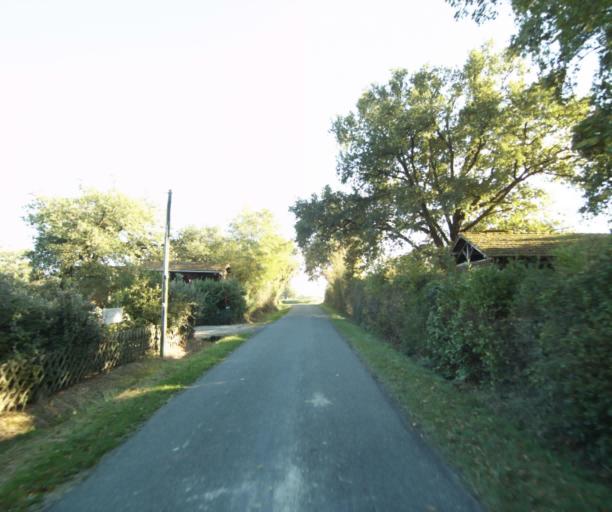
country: FR
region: Midi-Pyrenees
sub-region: Departement du Gers
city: Eauze
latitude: 43.7880
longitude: 0.1427
